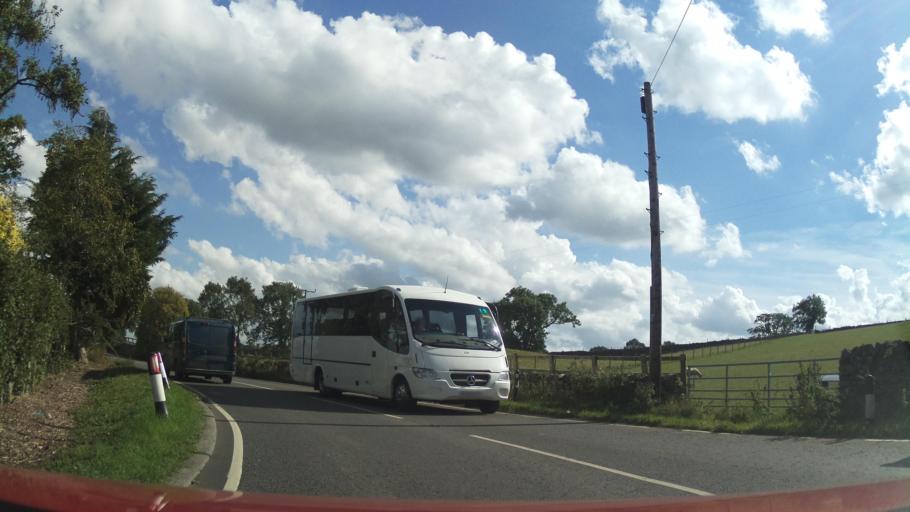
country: GB
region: England
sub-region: North Yorkshire
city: Leyburn
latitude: 54.2930
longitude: -1.8183
